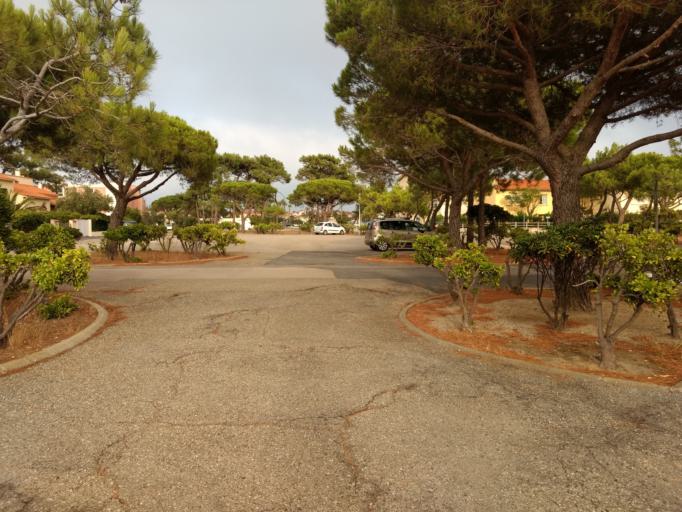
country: FR
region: Languedoc-Roussillon
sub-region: Departement des Pyrenees-Orientales
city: Le Barcares
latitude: 42.7890
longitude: 3.0326
